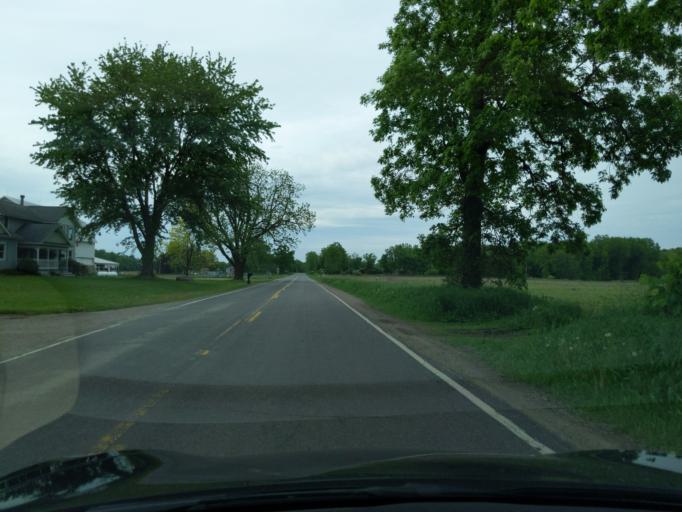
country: US
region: Michigan
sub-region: Ingham County
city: Leslie
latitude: 42.4579
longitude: -84.3512
